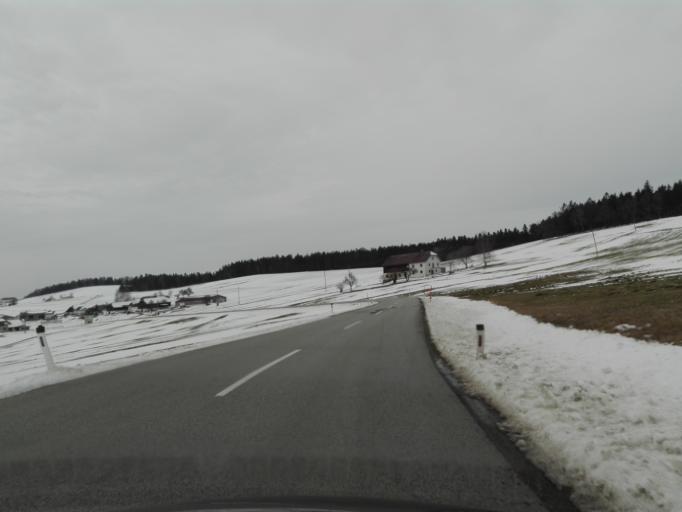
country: AT
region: Upper Austria
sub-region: Politischer Bezirk Rohrbach
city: Pfarrkirchen im Muehlkreis
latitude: 48.5556
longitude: 13.8150
